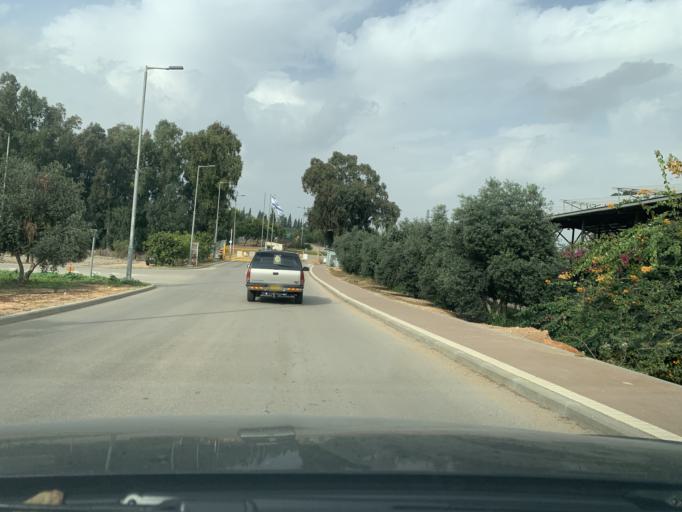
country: IL
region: Central District
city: Tirah
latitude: 32.2195
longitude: 34.9394
